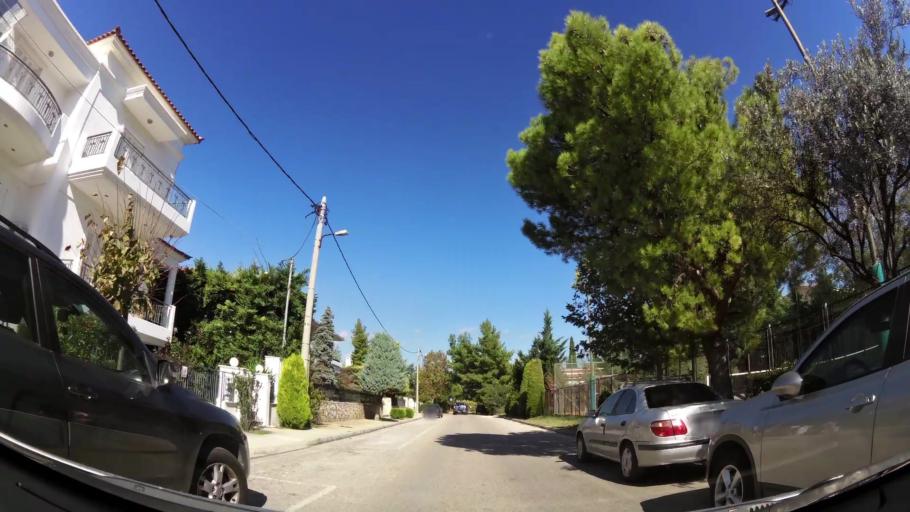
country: GR
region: Attica
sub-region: Nomarchia Athinas
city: Lykovrysi
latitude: 38.0755
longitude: 23.7928
